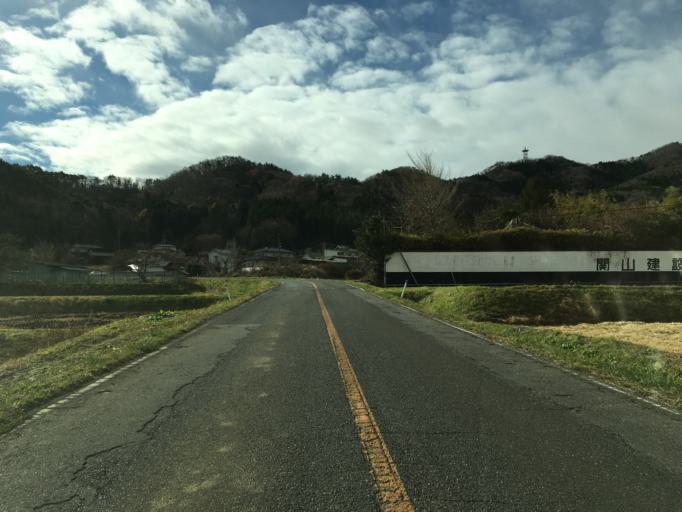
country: JP
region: Fukushima
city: Motomiya
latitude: 37.5201
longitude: 140.3697
